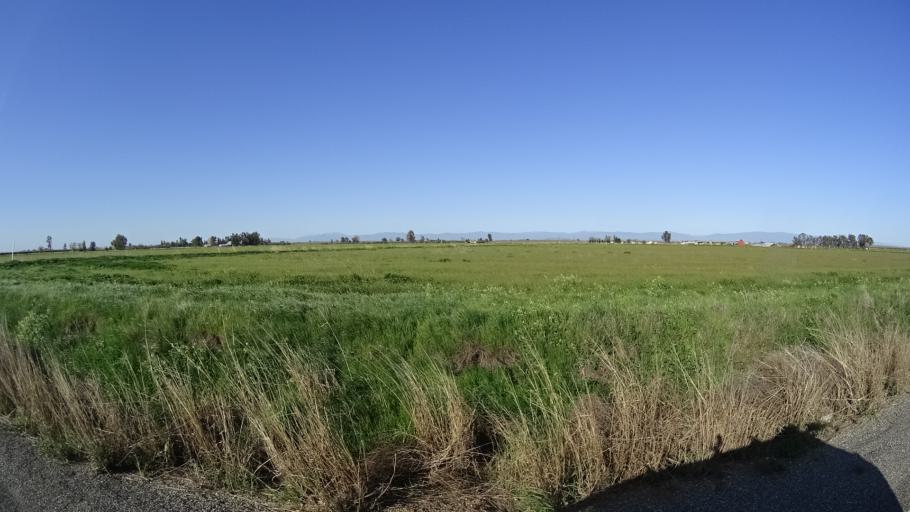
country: US
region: California
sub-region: Glenn County
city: Orland
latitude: 39.7747
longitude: -122.1132
